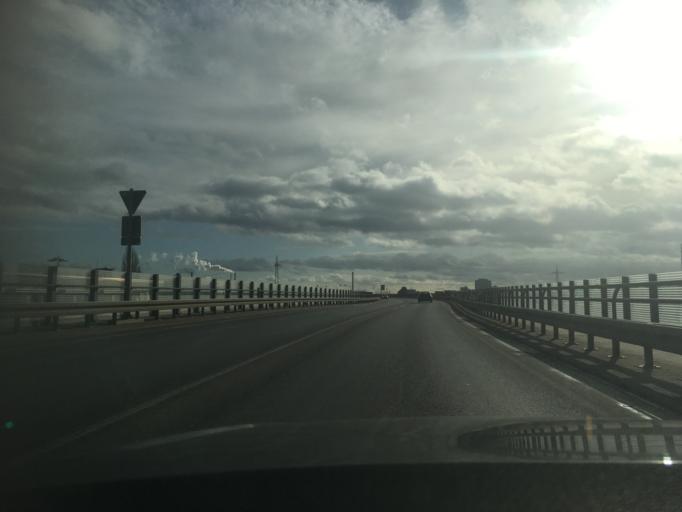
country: DE
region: North Rhine-Westphalia
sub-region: Regierungsbezirk Koln
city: Hurth
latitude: 50.8826
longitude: 6.9070
